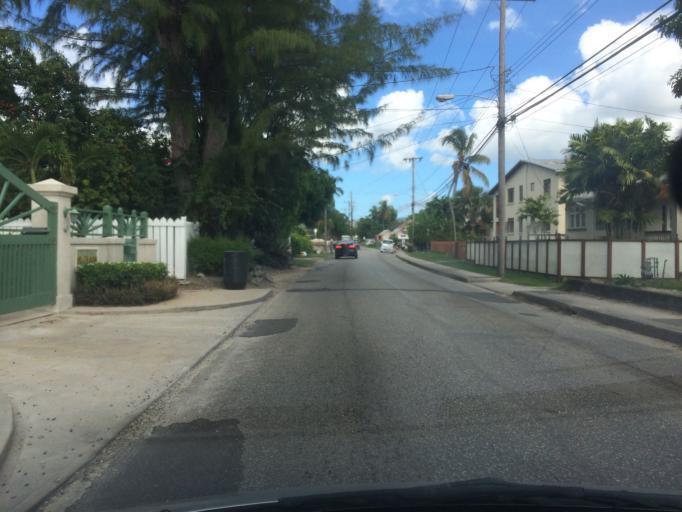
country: BB
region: Saint James
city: Holetown
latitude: 13.1487
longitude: -59.6381
